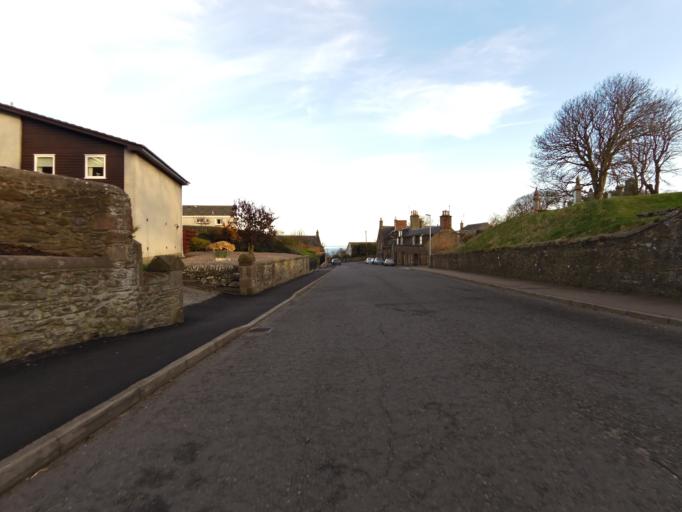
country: GB
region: Scotland
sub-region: Aberdeenshire
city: Inverbervie
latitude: 56.8442
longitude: -2.2790
